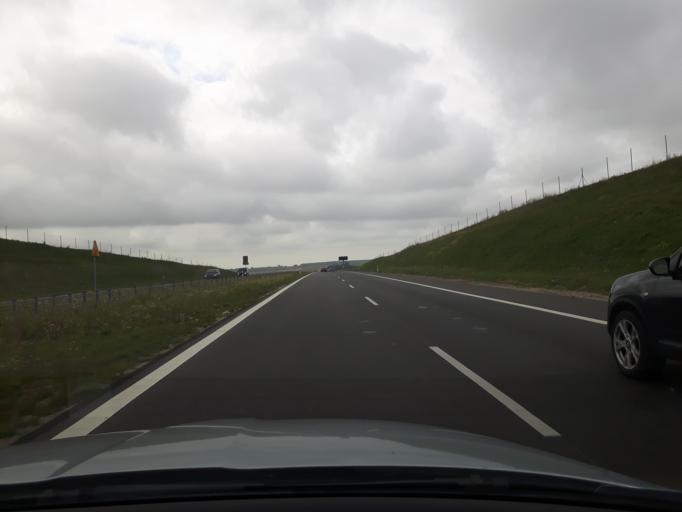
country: PL
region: Swietokrzyskie
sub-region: Powiat jedrzejowski
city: Sobkow
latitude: 50.7162
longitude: 20.4084
